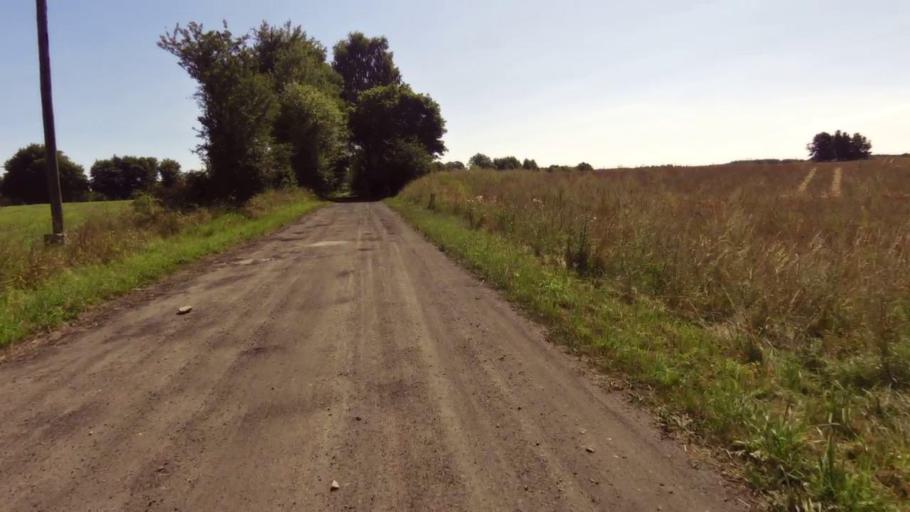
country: PL
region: West Pomeranian Voivodeship
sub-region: Powiat drawski
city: Zlocieniec
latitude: 53.5226
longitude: 16.0344
